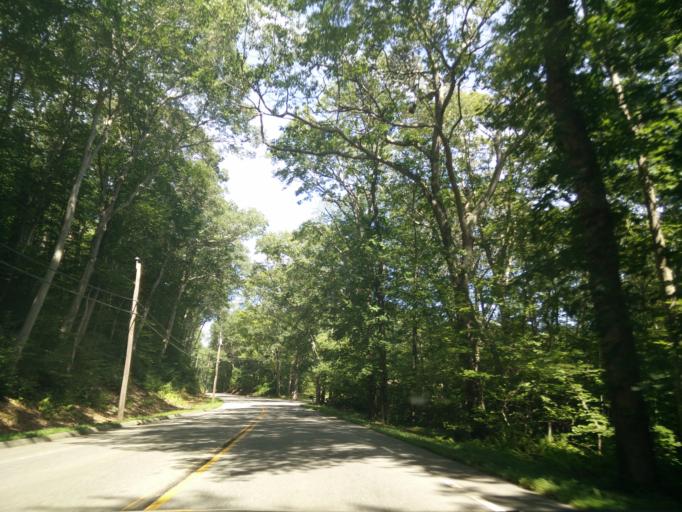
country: US
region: Connecticut
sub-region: Middlesex County
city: Clinton
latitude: 41.3282
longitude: -72.5498
